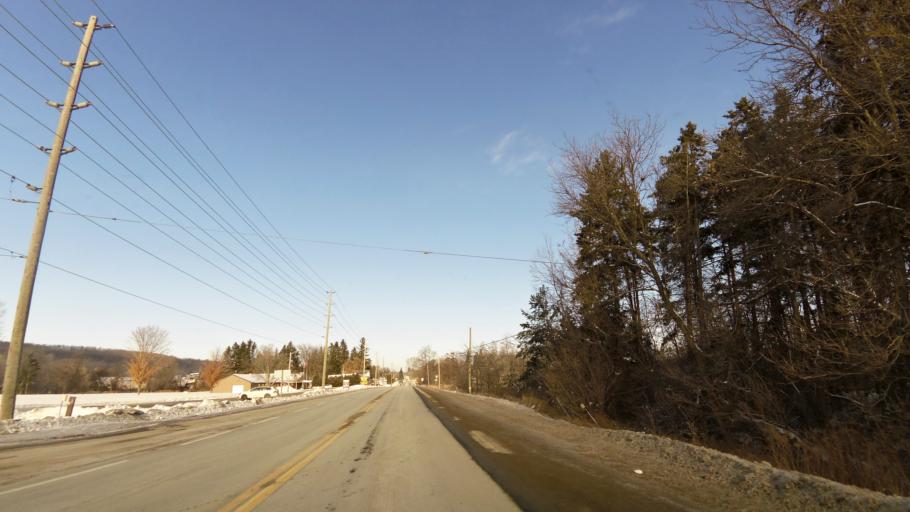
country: CA
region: Ontario
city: Quinte West
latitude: 44.1581
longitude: -77.7992
